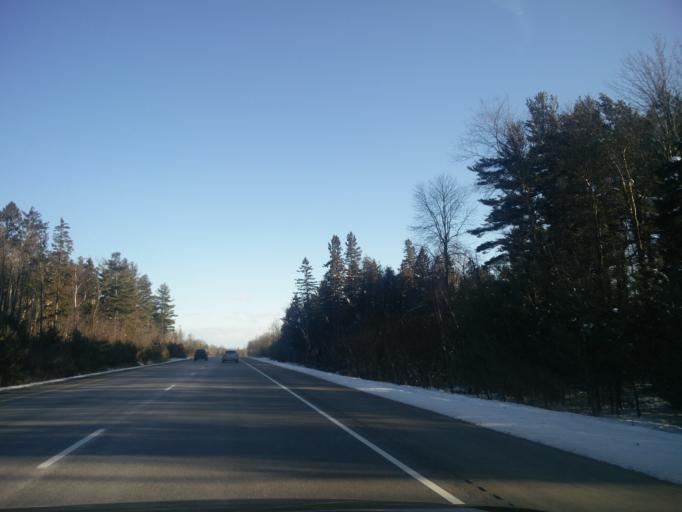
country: CA
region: Ontario
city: Prescott
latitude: 44.8297
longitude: -75.5256
